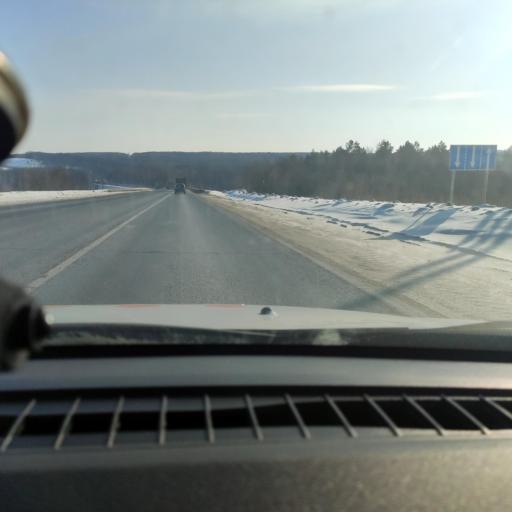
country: RU
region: Samara
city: Novosemeykino
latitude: 53.3632
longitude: 50.4377
